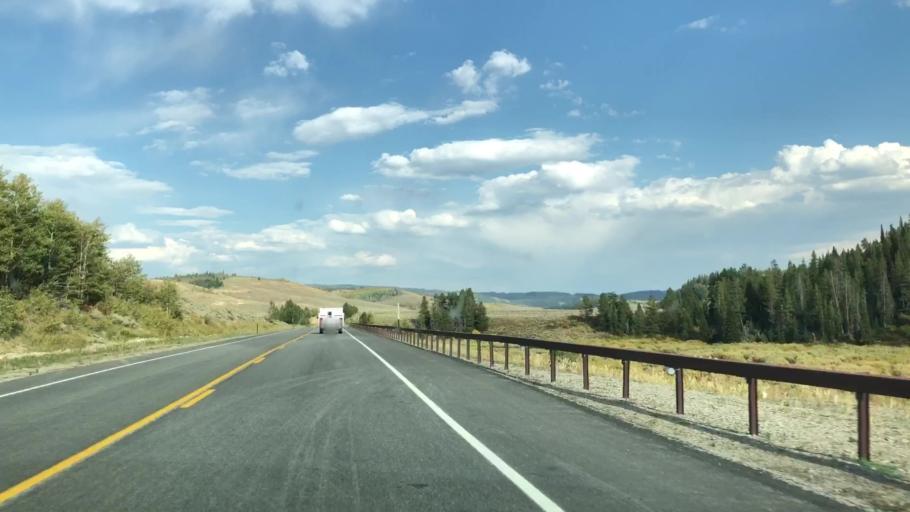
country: US
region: Wyoming
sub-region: Teton County
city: Hoback
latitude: 43.1562
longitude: -110.3125
